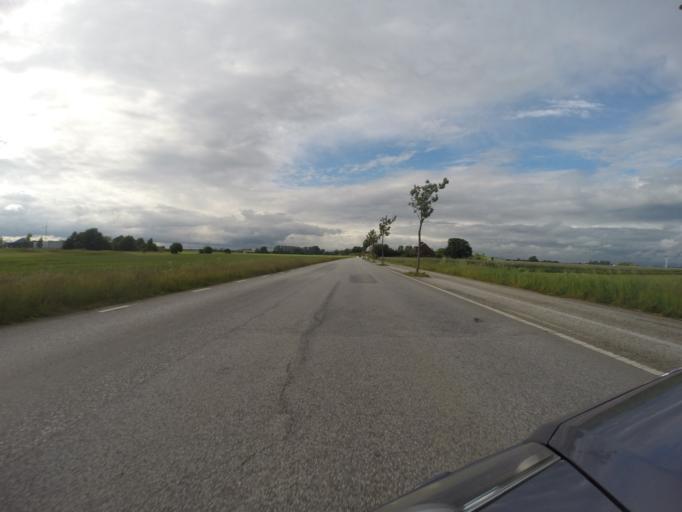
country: SE
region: Skane
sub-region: Kavlinge Kommun
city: Loddekopinge
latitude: 55.7696
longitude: 13.0117
